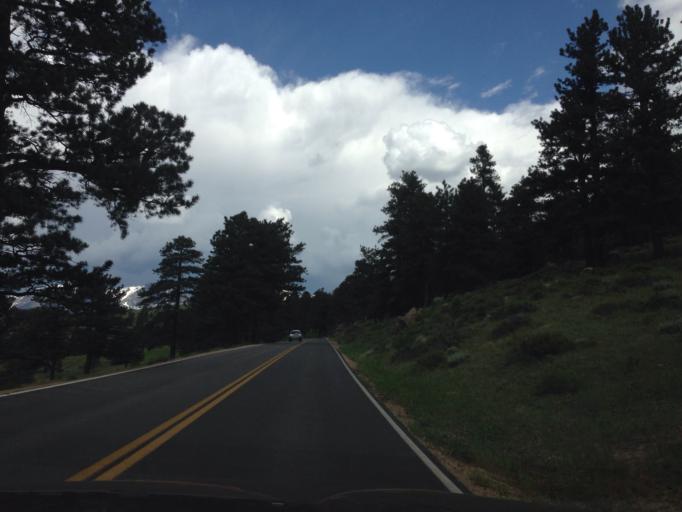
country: US
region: Colorado
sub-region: Larimer County
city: Estes Park
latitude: 40.3766
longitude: -105.5966
